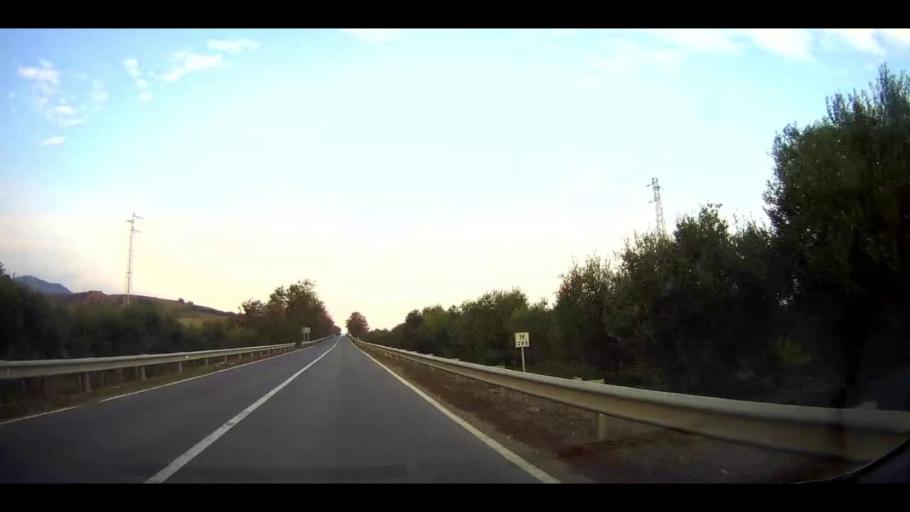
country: IT
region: Calabria
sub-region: Provincia di Crotone
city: Torretta
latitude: 39.4718
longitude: 17.0144
